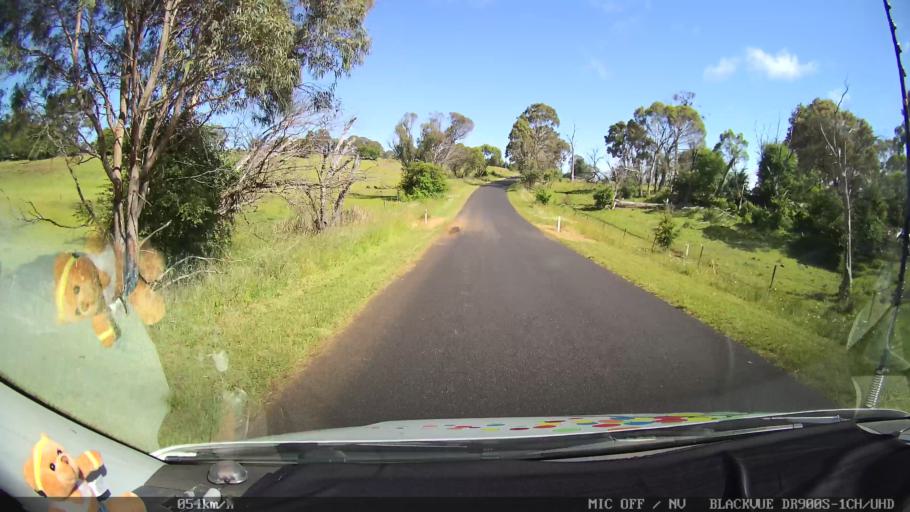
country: AU
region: New South Wales
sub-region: Guyra
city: Guyra
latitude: -30.1075
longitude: 151.6799
